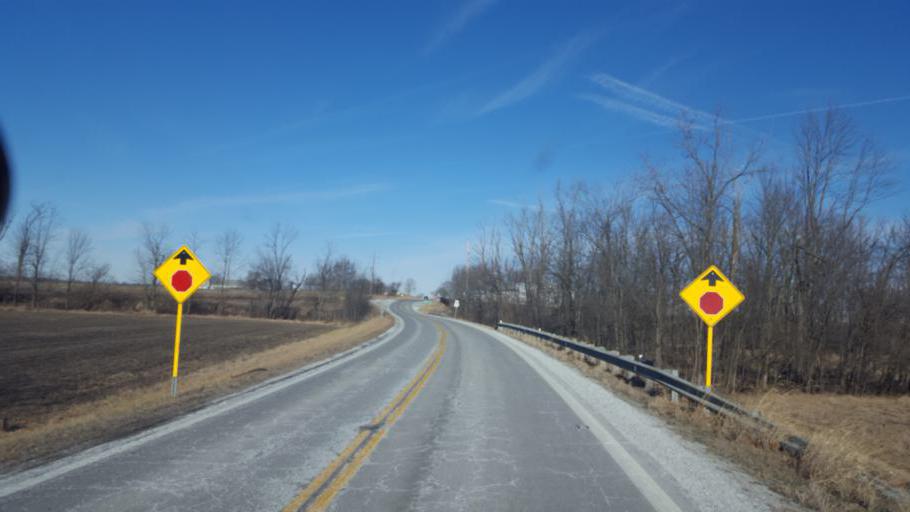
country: US
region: Ohio
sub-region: Marion County
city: Marion
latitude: 40.5473
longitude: -83.1900
